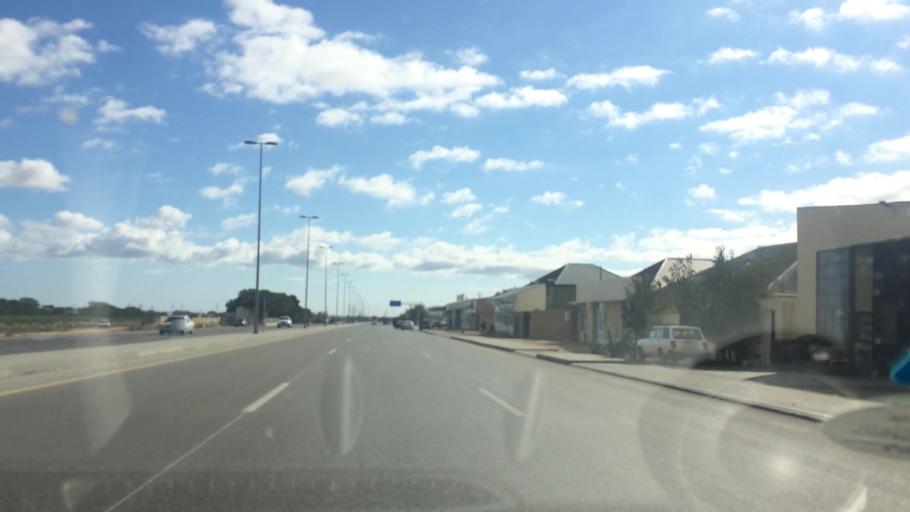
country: AZ
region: Baki
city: Qala
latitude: 40.4468
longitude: 50.1685
